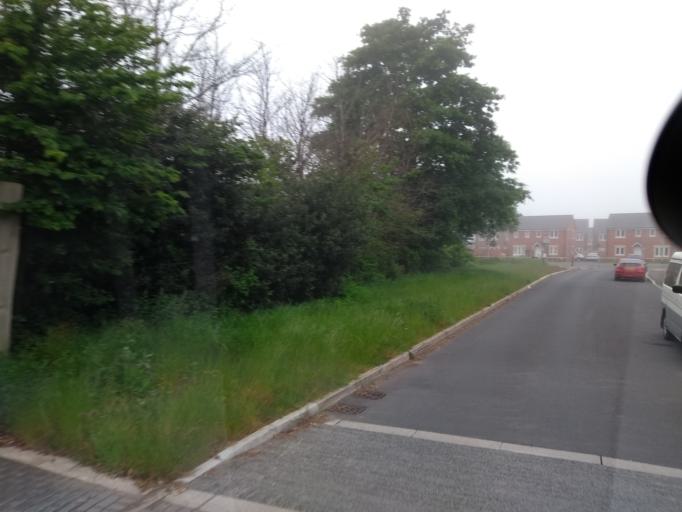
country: GB
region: England
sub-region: Somerset
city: Creech Saint Michael
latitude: 51.0366
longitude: -3.0552
